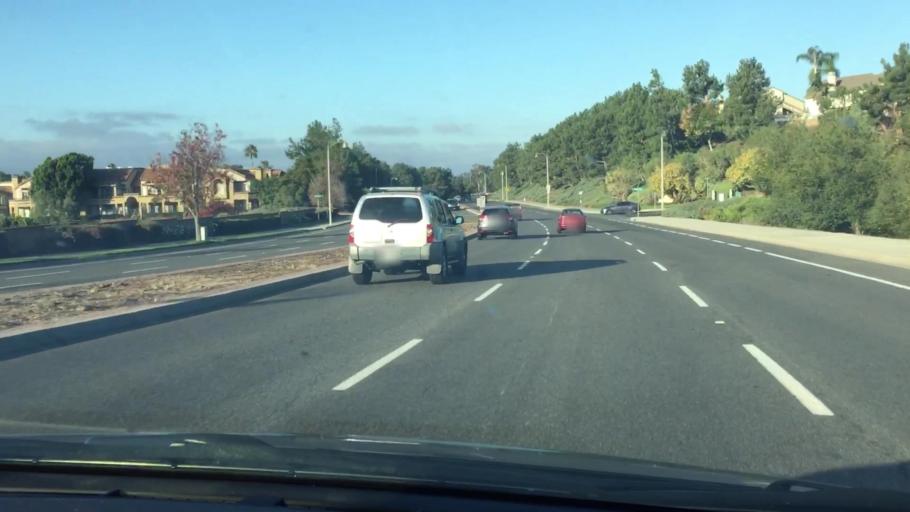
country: US
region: California
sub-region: Orange County
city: Portola Hills
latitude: 33.6510
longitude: -117.6381
